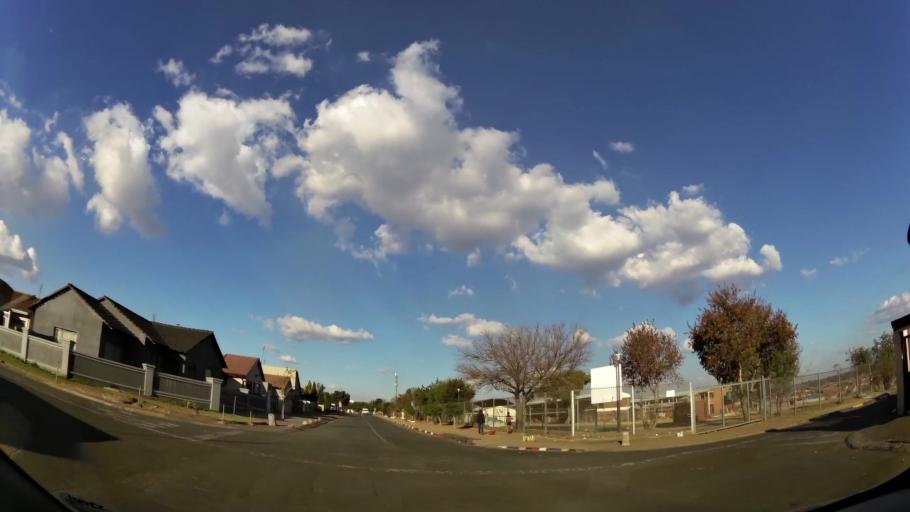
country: ZA
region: Mpumalanga
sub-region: Nkangala District Municipality
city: Witbank
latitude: -25.8741
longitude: 29.1761
